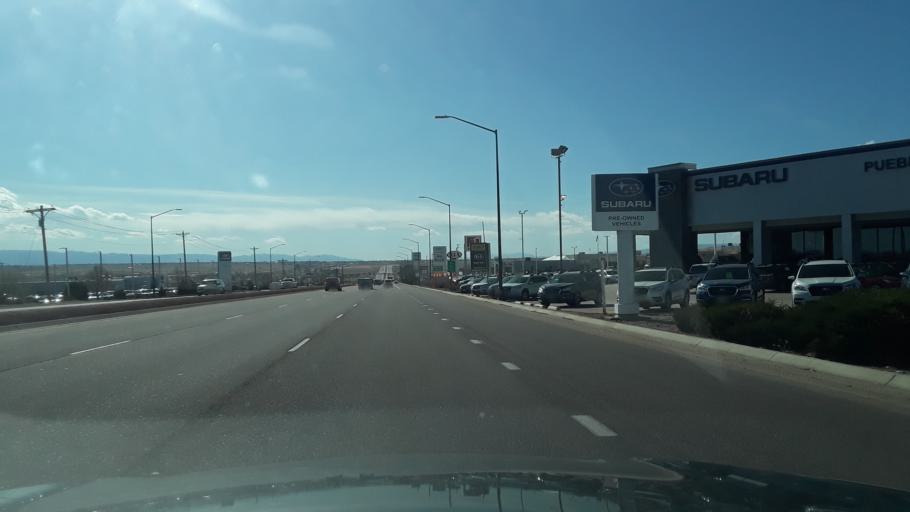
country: US
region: Colorado
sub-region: Pueblo County
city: Pueblo
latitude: 38.3105
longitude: -104.6359
